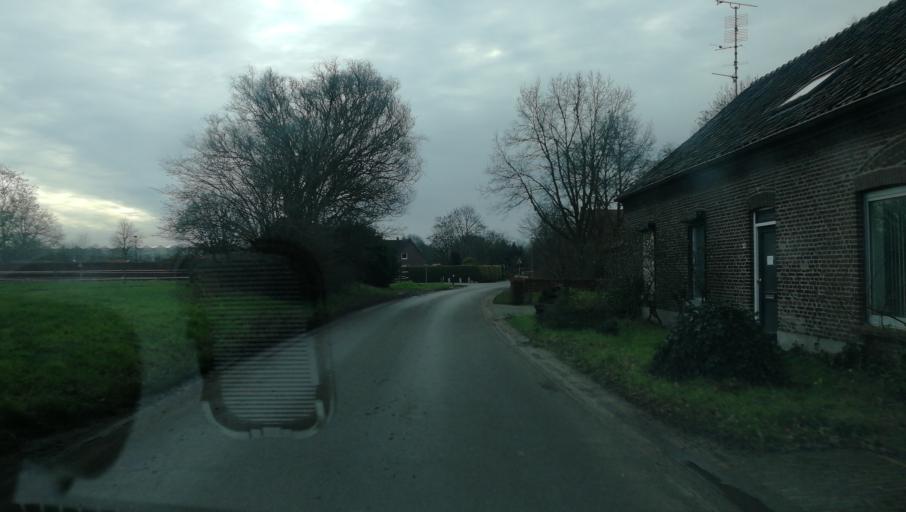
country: NL
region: Limburg
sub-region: Gemeente Venlo
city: Arcen
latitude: 51.4218
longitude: 6.1891
